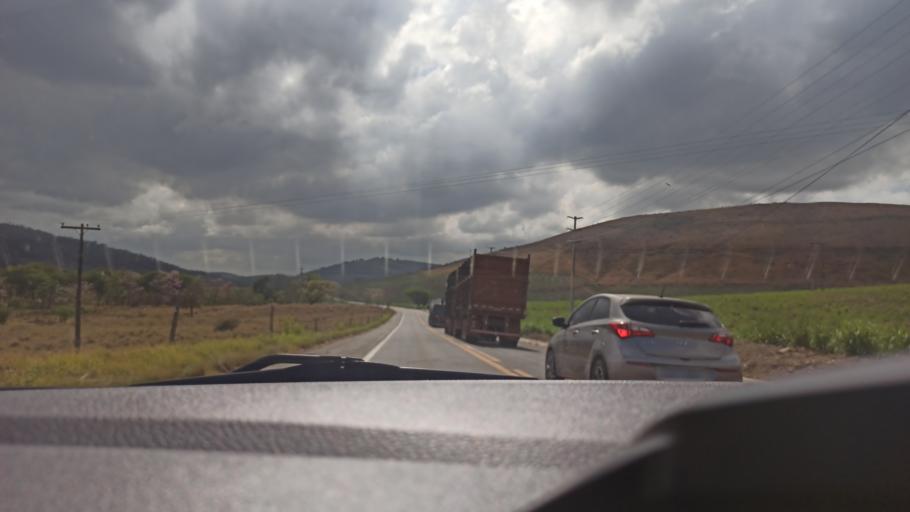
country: BR
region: Pernambuco
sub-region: Timbauba
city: Timbauba
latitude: -7.5219
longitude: -35.3018
